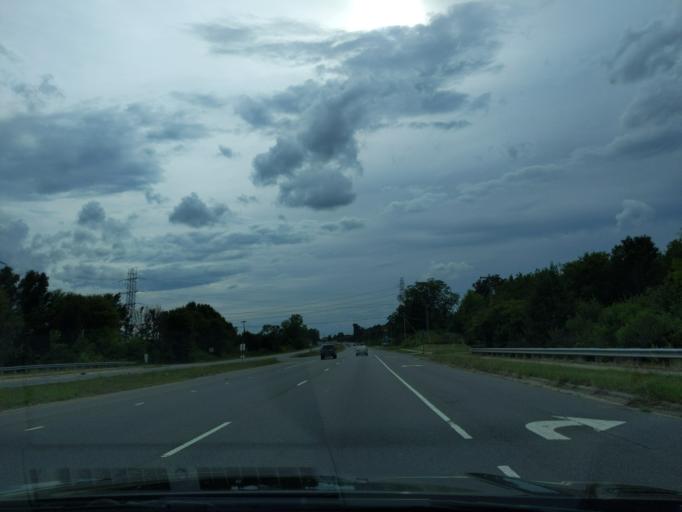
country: US
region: North Carolina
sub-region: Cabarrus County
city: Harrisburg
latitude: 35.3154
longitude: -80.6903
